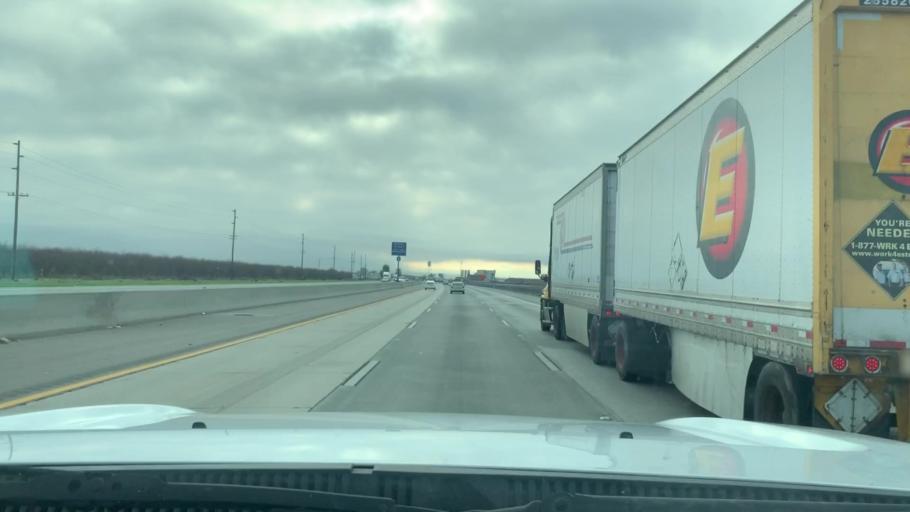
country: US
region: California
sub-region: Kern County
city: Shafter
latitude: 35.5104
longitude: -119.1774
